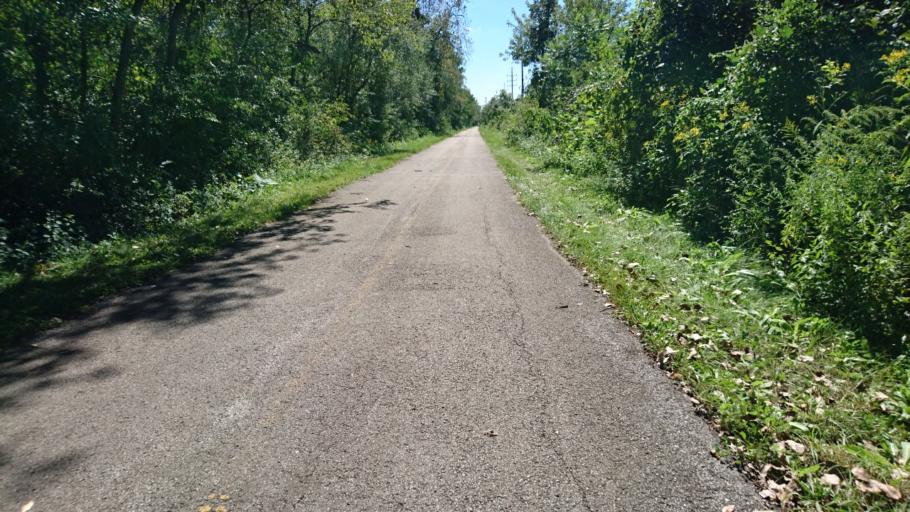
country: US
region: Illinois
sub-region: Cook County
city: Glenwood
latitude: 41.5341
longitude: -87.6227
